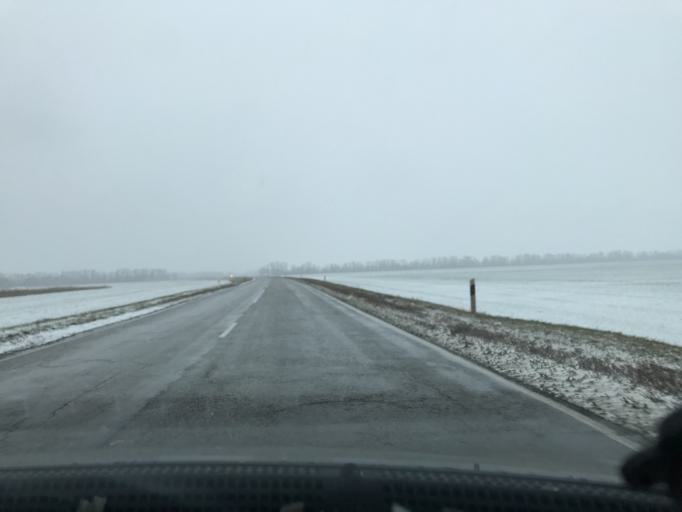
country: RU
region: Rostov
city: Yegorlykskaya
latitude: 46.5410
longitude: 40.6696
